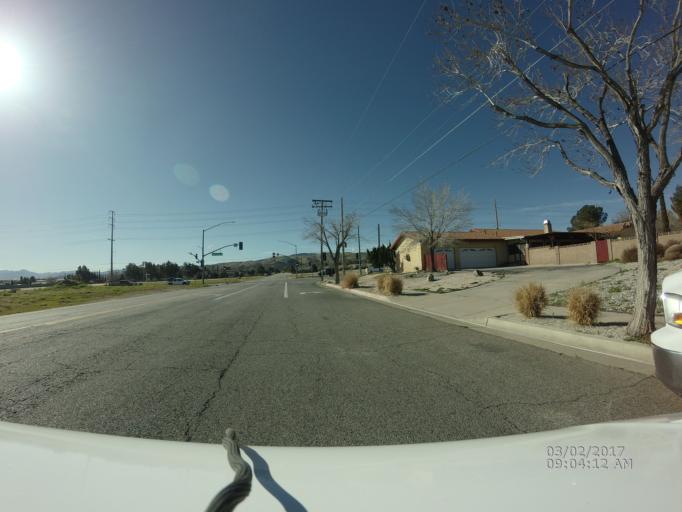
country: US
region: California
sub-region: Los Angeles County
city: Quartz Hill
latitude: 34.6314
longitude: -118.2100
